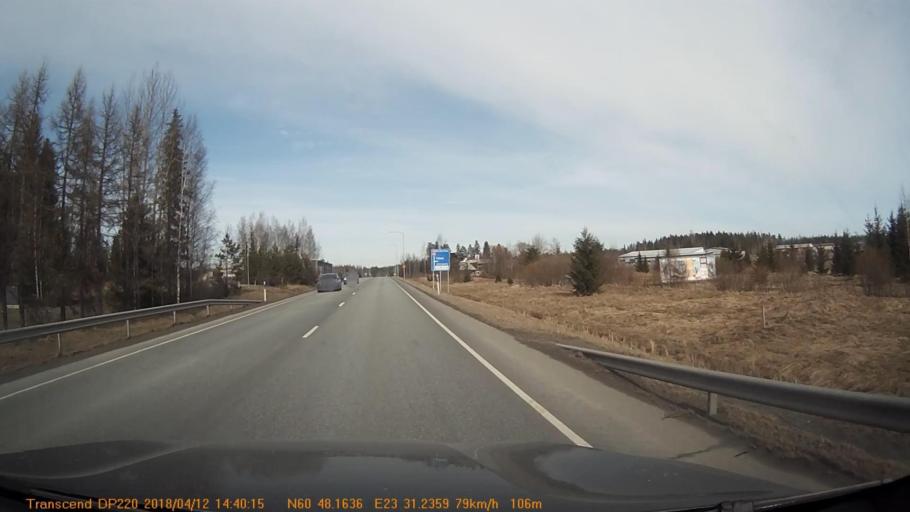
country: FI
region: Haeme
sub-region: Forssa
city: Jokioinen
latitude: 60.8039
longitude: 23.5229
